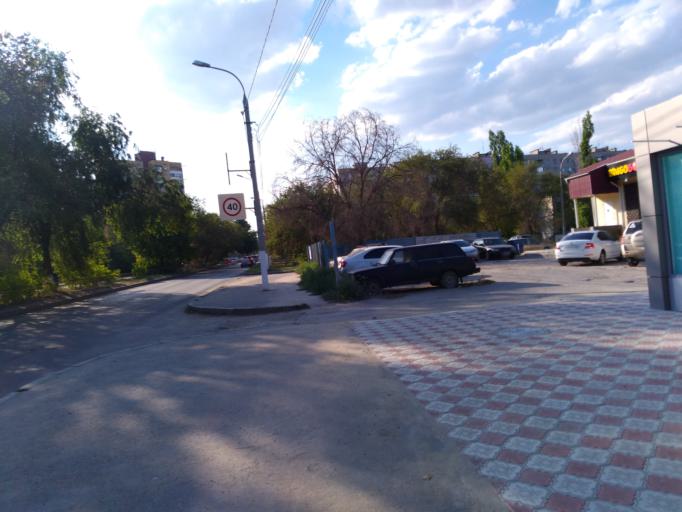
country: RU
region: Volgograd
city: Volgograd
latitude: 48.7203
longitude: 44.5143
